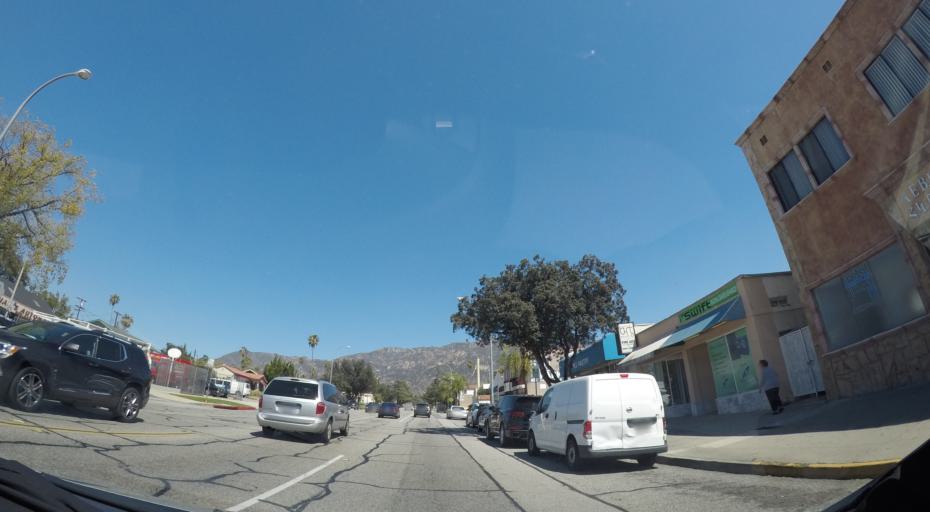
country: US
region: California
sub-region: Los Angeles County
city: East Pasadena
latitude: 34.1644
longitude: -118.1131
